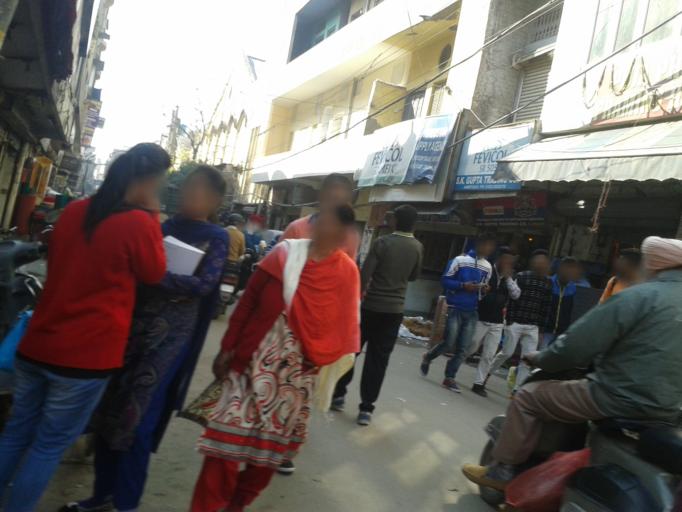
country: IN
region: Punjab
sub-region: Amritsar
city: Amritsar
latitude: 31.6292
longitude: 74.8738
